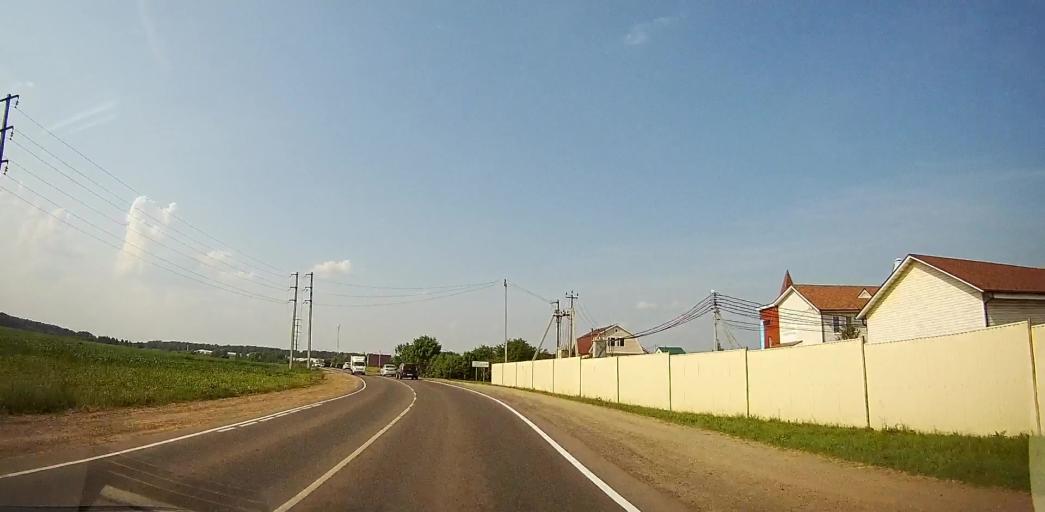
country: RU
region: Moskovskaya
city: Barybino
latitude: 55.2966
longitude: 37.9124
